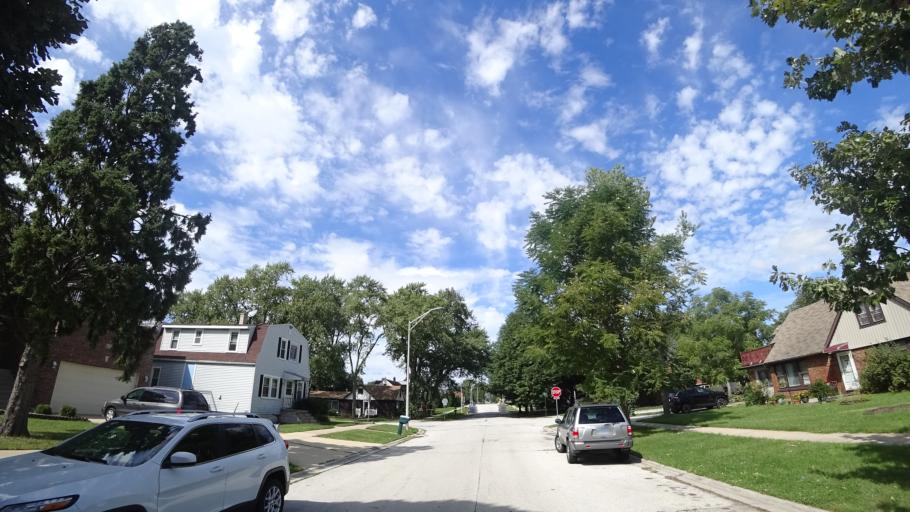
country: US
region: Illinois
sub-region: Cook County
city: Chicago Ridge
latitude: 41.7138
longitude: -87.7724
